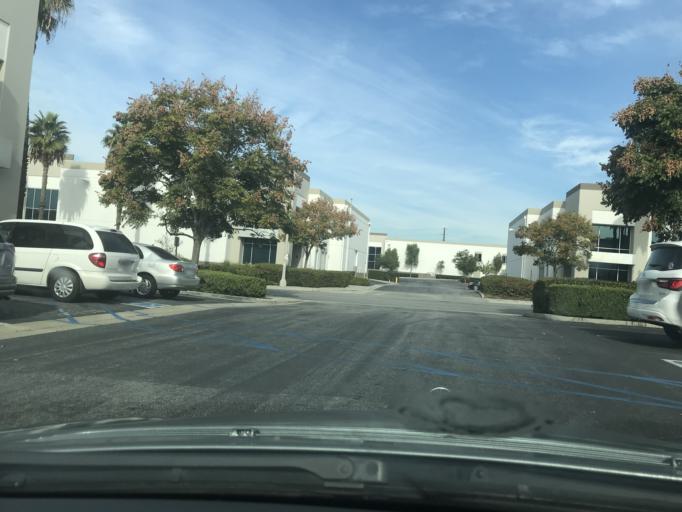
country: US
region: California
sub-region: Los Angeles County
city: Santa Fe Springs
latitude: 33.9334
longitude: -118.0632
